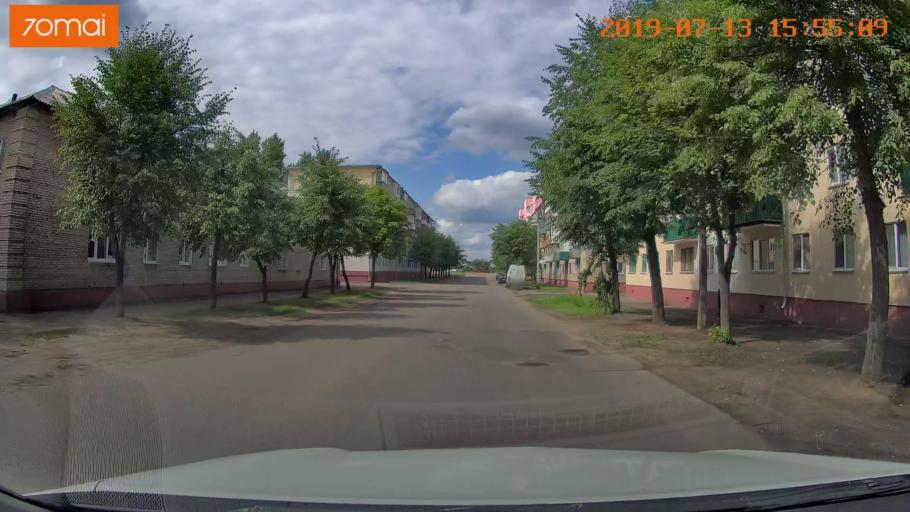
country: BY
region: Mogilev
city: Babruysk
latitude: 53.1401
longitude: 29.1989
